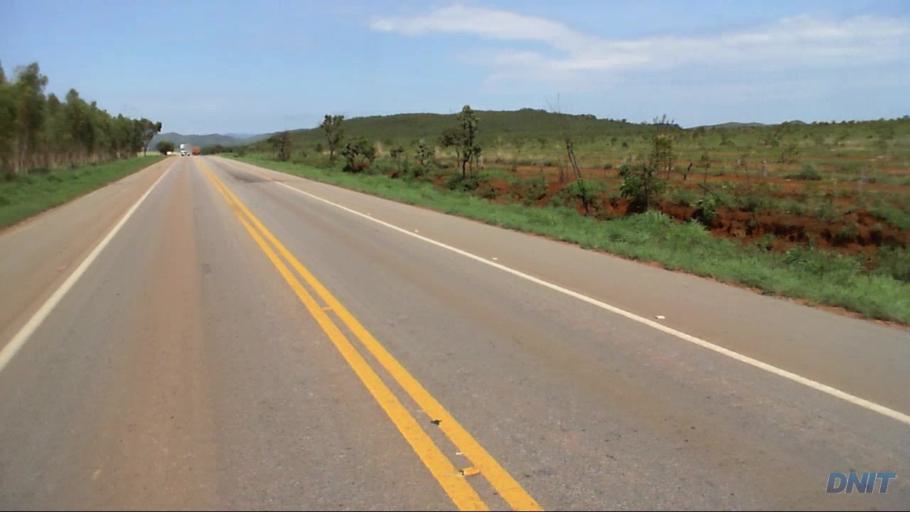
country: BR
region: Goias
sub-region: Barro Alto
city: Barro Alto
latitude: -15.2036
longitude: -48.7425
